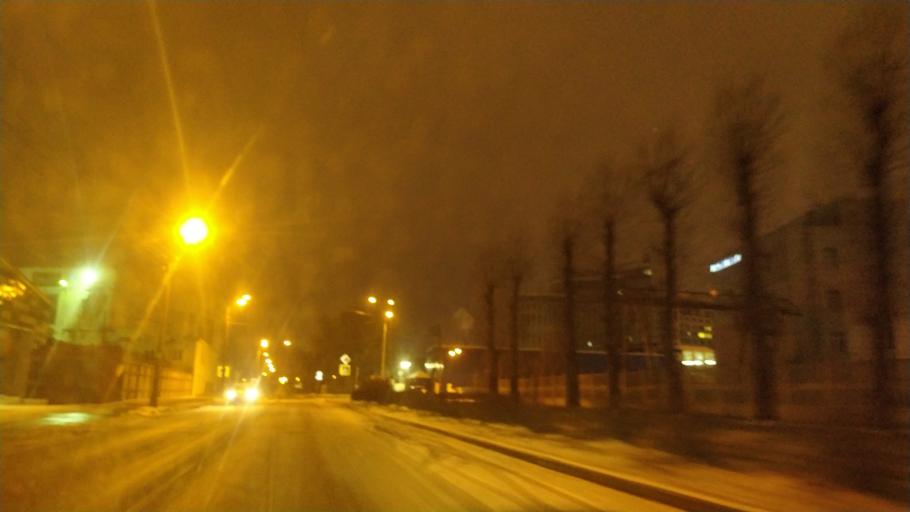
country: RU
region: St.-Petersburg
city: Kupchino
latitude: 59.8826
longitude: 30.3308
